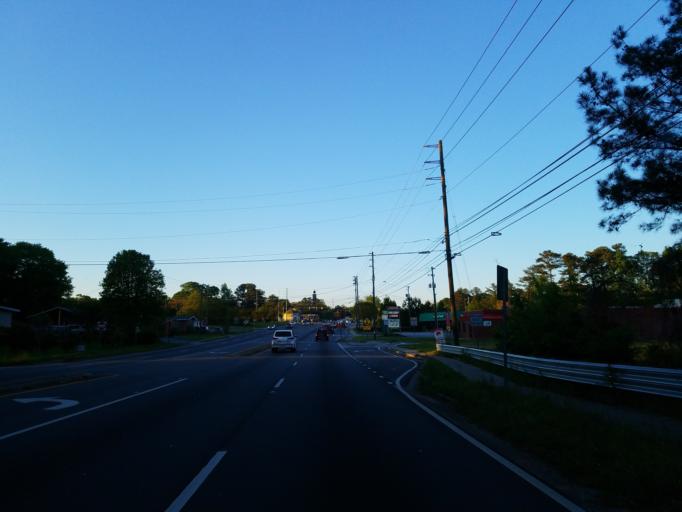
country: US
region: Georgia
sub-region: Cobb County
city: Fair Oaks
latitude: 33.8931
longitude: -84.5773
